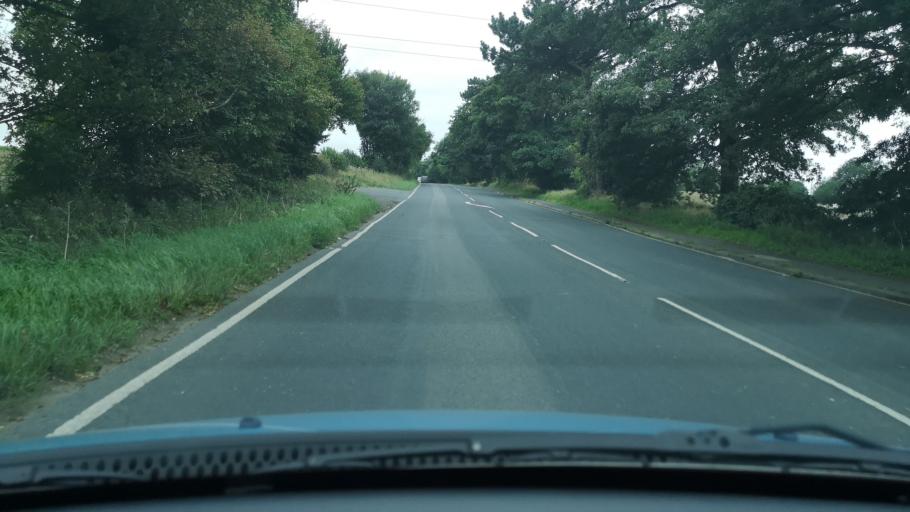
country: GB
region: England
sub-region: City and Borough of Wakefield
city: Low Ackworth
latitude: 53.6698
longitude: -1.3237
